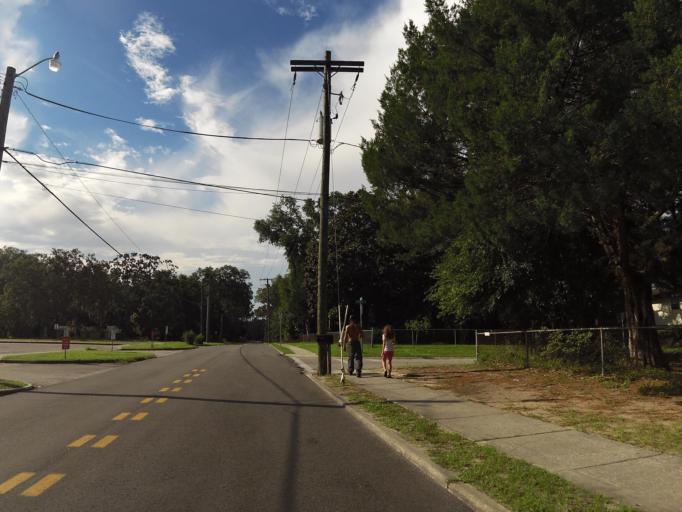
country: US
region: Florida
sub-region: Clay County
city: Green Cove Springs
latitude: 29.9893
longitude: -81.6974
